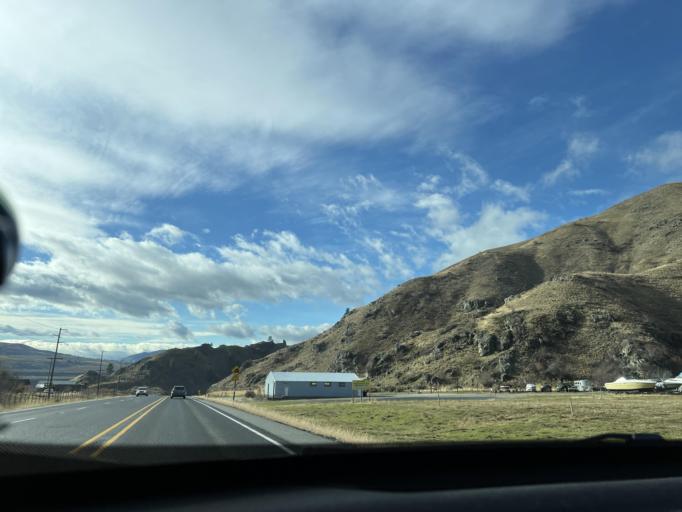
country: US
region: Washington
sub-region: Chelan County
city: Manson
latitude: 47.7848
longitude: -120.1384
